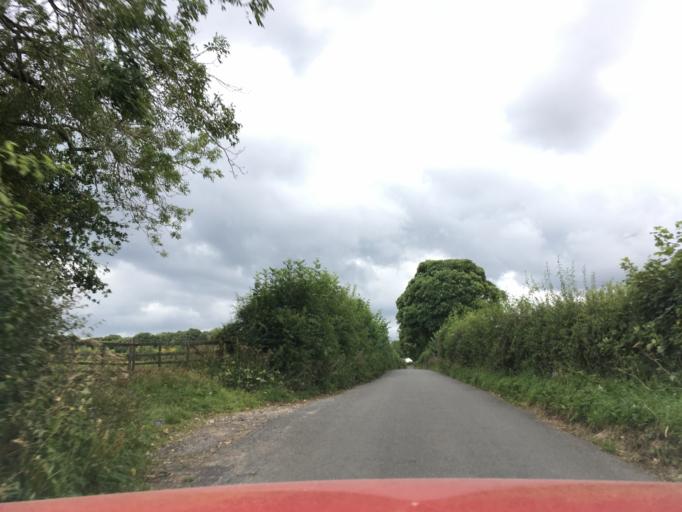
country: GB
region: England
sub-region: Gloucestershire
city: Chalford
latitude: 51.7577
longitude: -2.0868
